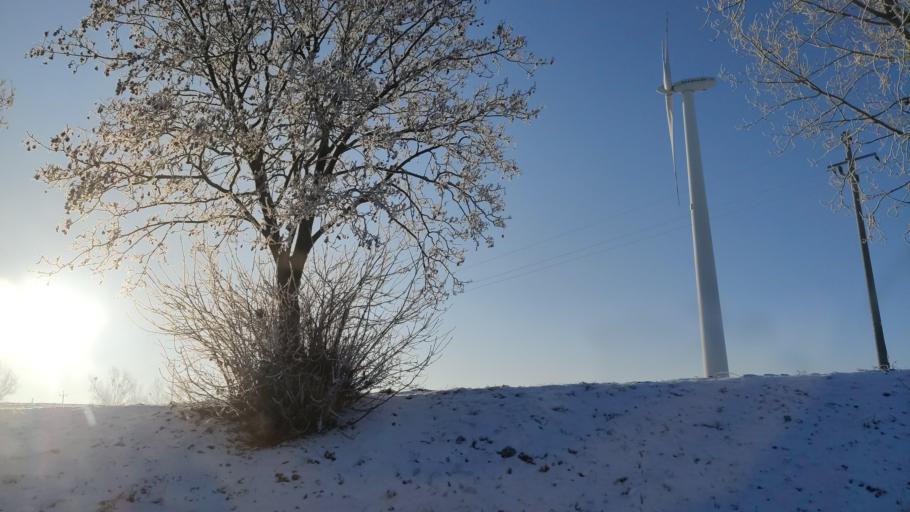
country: PL
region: Kujawsko-Pomorskie
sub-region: Powiat zninski
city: Barcin
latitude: 52.8717
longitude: 17.8469
